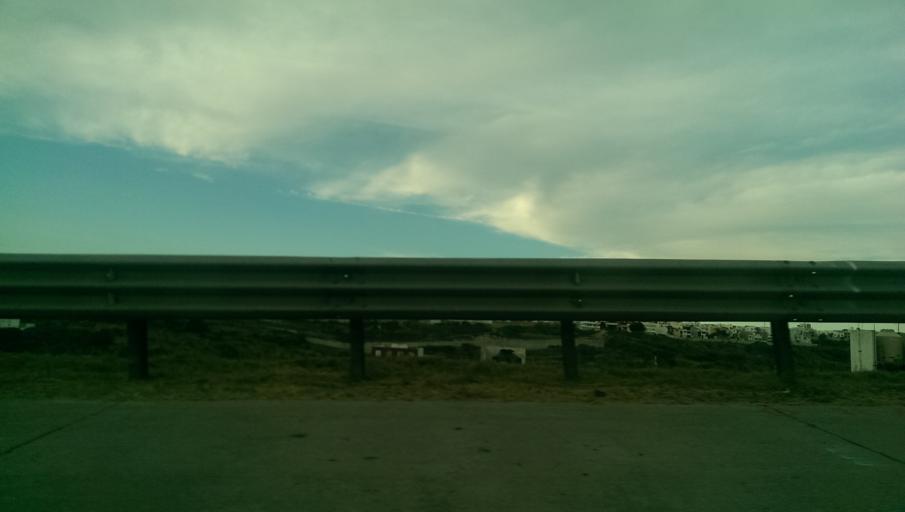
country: MX
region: Queretaro
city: La Canada
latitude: 20.5875
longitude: -100.3462
